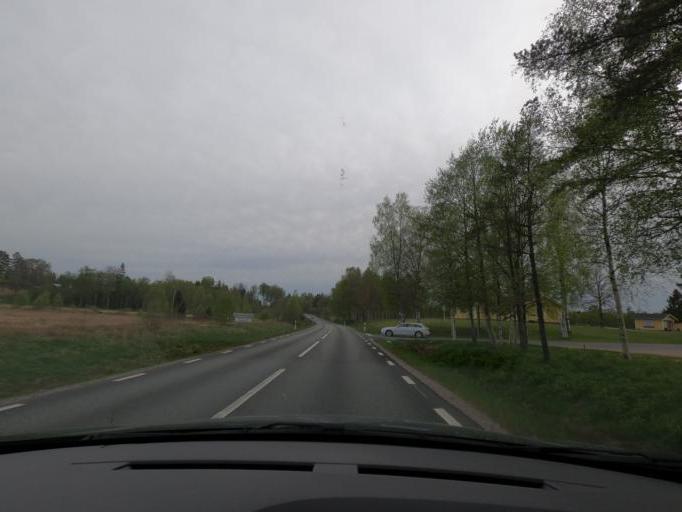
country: SE
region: Joenkoeping
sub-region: Varnamo Kommun
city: Bredaryd
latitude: 57.2128
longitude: 13.7693
